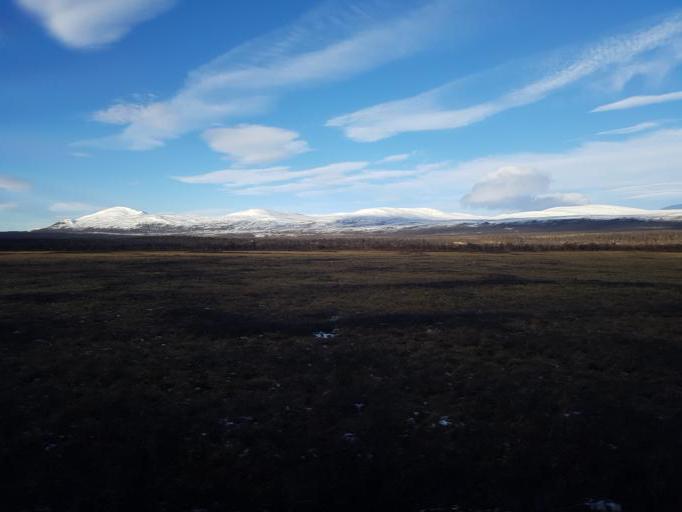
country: NO
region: Oppland
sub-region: Dovre
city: Dovre
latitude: 62.1411
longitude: 9.3270
